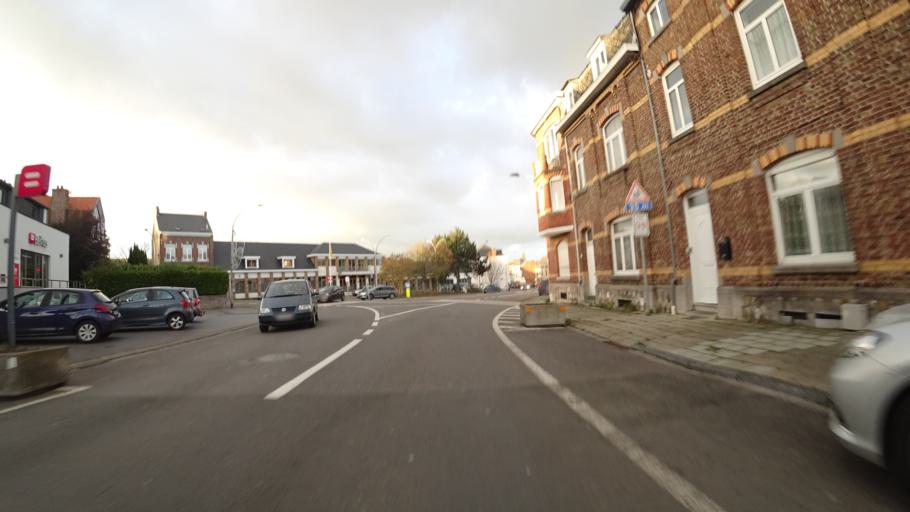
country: BE
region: Wallonia
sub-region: Province de Namur
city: Namur
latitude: 50.4702
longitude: 4.8255
